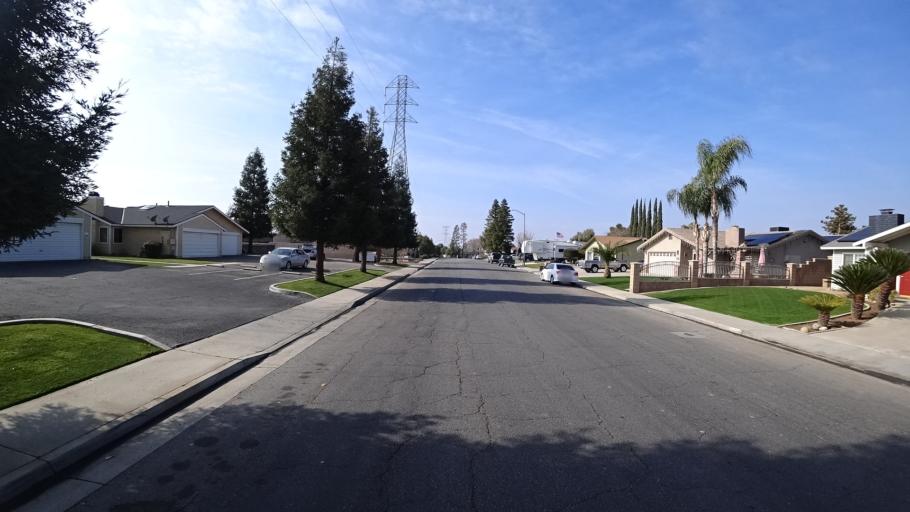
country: US
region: California
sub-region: Kern County
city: Oildale
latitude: 35.3990
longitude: -118.9278
